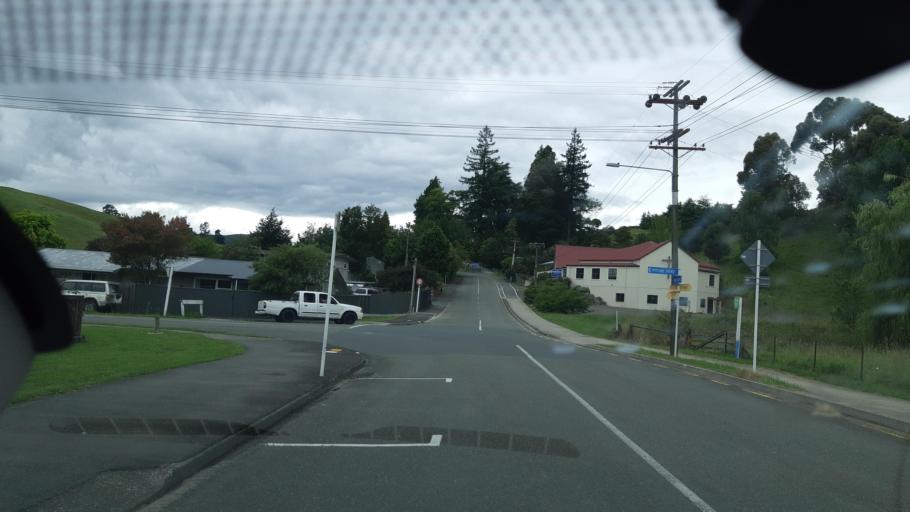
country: NZ
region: Tasman
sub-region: Tasman District
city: Wakefield
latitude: -41.4082
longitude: 173.0455
